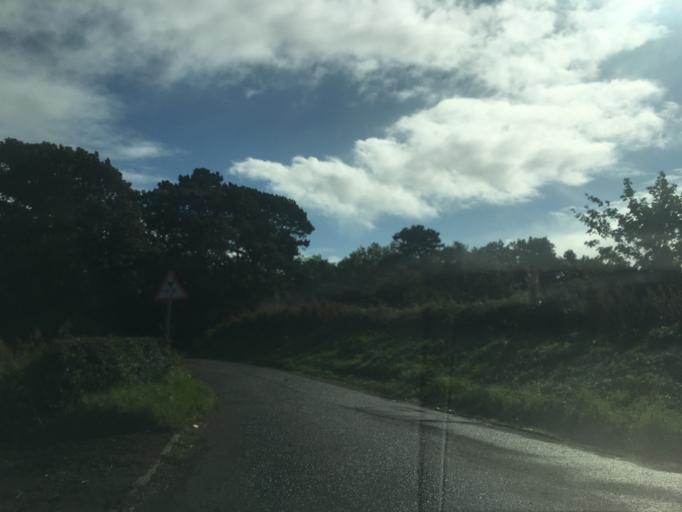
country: GB
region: Scotland
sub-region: Edinburgh
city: Kirkliston
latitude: 55.9650
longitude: -3.3793
